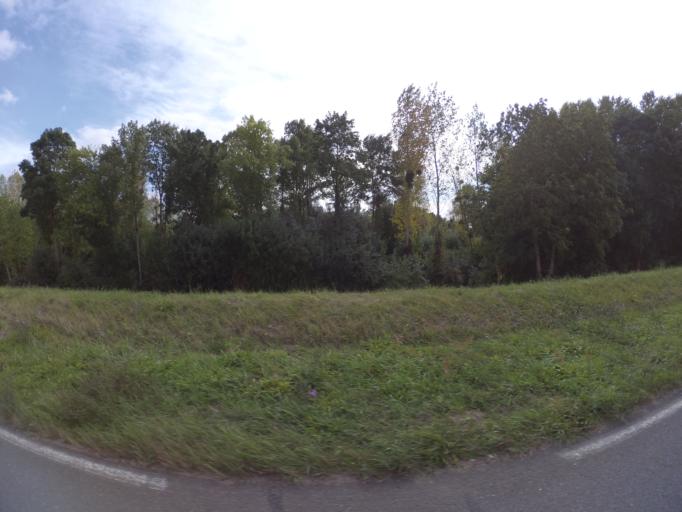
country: FR
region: Centre
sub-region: Departement d'Indre-et-Loire
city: Huismes
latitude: 47.2682
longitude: 0.2905
